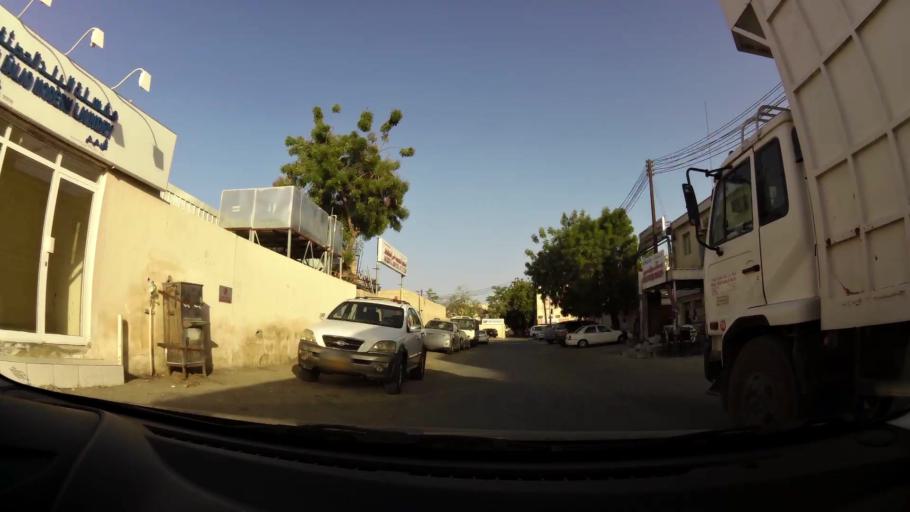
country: OM
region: Muhafazat Masqat
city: Muscat
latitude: 23.5876
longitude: 58.5557
